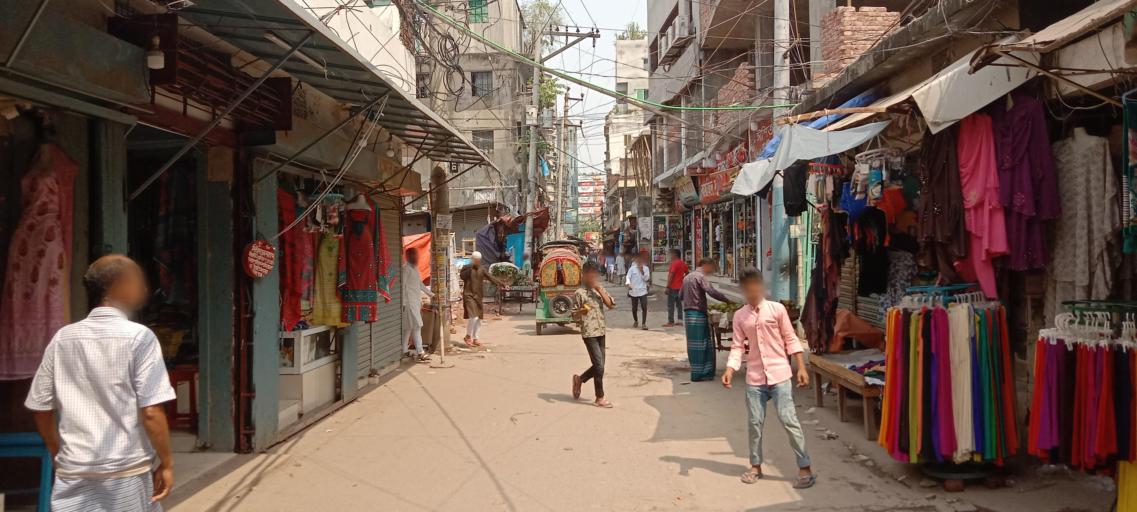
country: BD
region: Dhaka
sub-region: Dhaka
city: Dhaka
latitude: 23.7078
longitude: 90.3982
